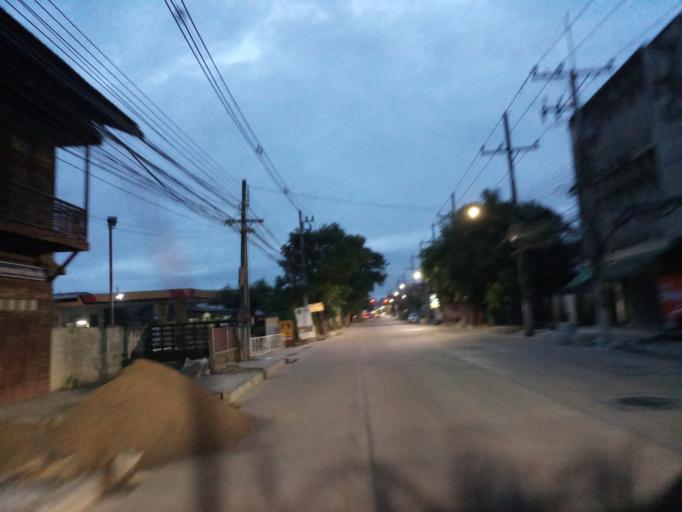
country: TH
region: Chiang Rai
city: Chiang Rai
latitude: 19.8993
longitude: 99.8323
